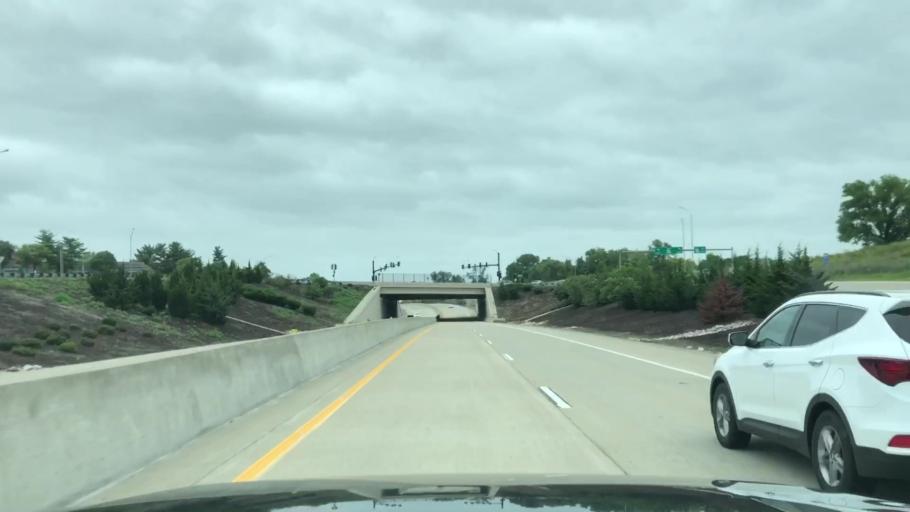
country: US
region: Missouri
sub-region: Saint Louis County
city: Maryland Heights
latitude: 38.6793
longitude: -90.4933
